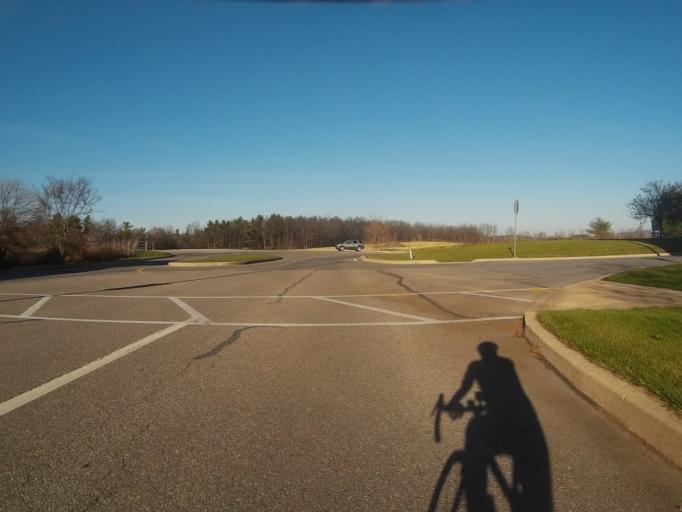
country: US
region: Pennsylvania
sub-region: Centre County
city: Houserville
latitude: 40.8333
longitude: -77.8417
